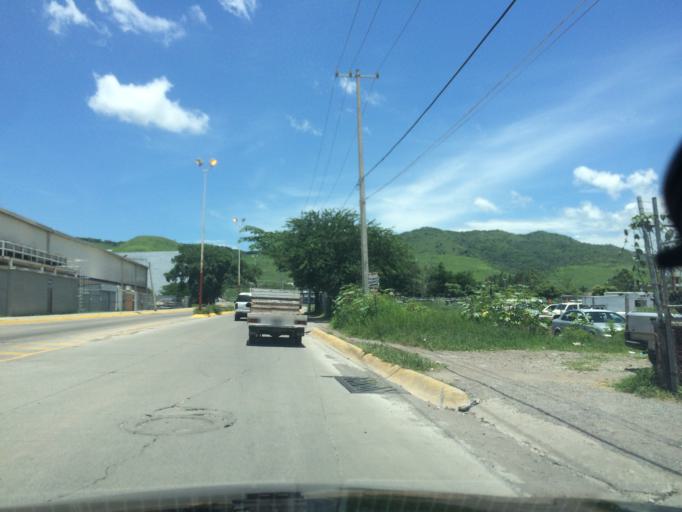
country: MX
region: Nayarit
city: Tepic
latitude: 21.4900
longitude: -104.8637
